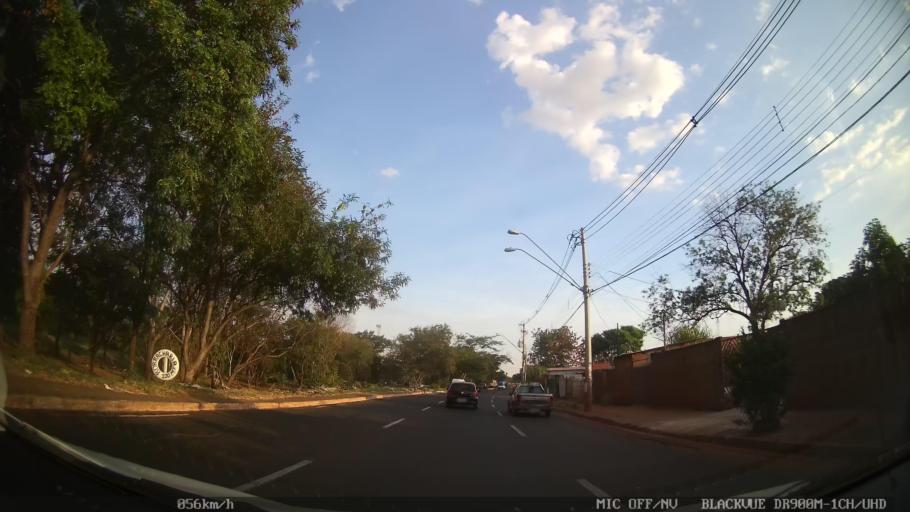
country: BR
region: Sao Paulo
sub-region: Ribeirao Preto
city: Ribeirao Preto
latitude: -21.1436
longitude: -47.8037
